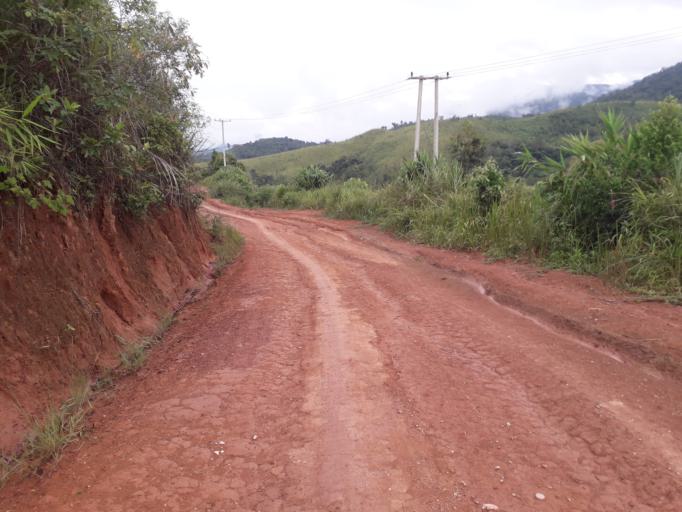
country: CN
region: Yunnan
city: Menglie
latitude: 22.2650
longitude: 101.5783
